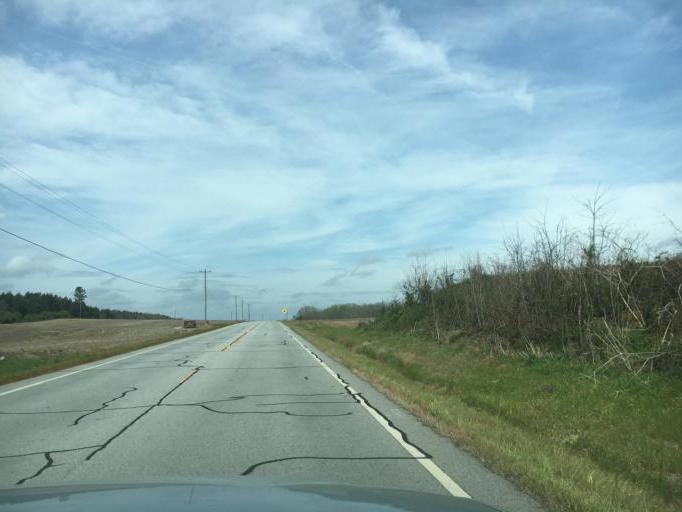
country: US
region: Georgia
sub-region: Franklin County
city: Lavonia
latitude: 34.4175
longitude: -83.0630
